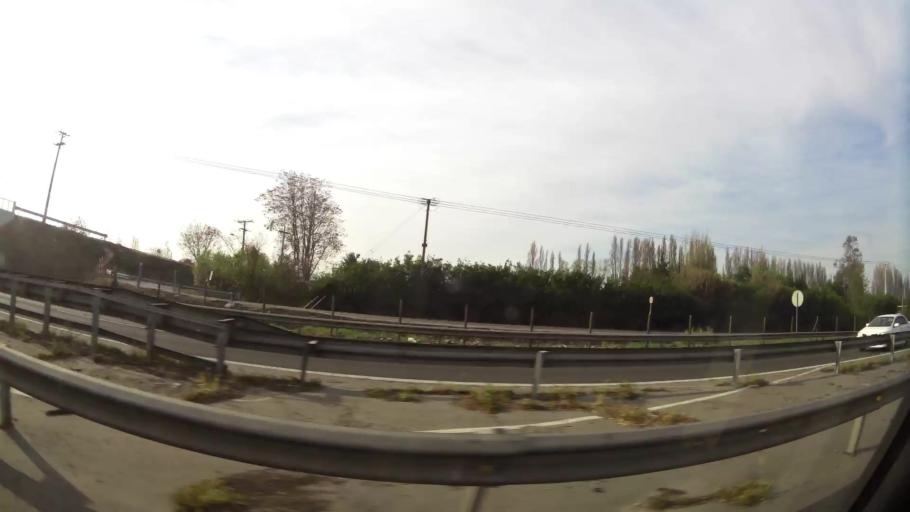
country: CL
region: Santiago Metropolitan
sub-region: Provincia de Talagante
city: Talagante
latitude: -33.6527
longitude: -70.8855
